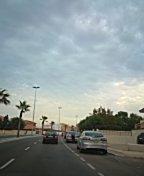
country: ES
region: Murcia
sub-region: Murcia
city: La Manga del Mar Menor
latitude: 37.6863
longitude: -0.7360
